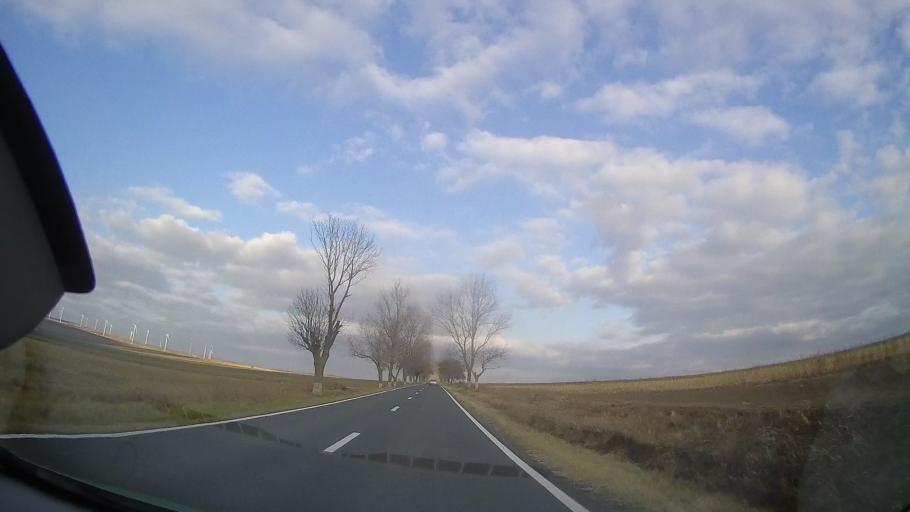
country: RO
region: Tulcea
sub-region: Comuna Topolog
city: Topolog
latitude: 44.8601
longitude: 28.3442
